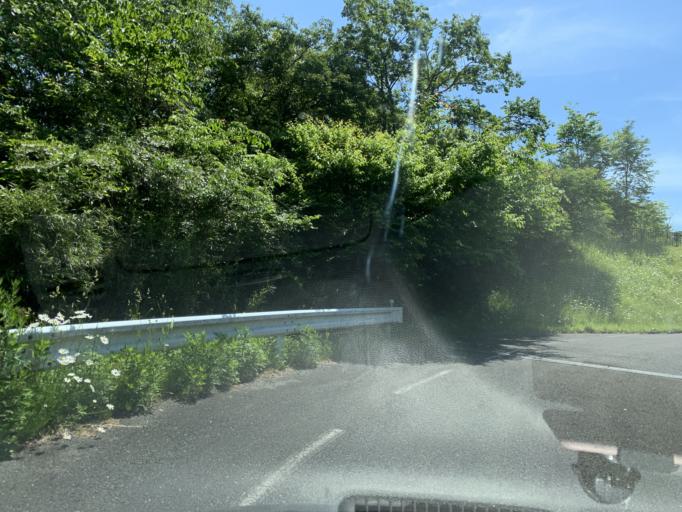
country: JP
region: Iwate
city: Ichinoseki
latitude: 38.9163
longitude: 141.1229
